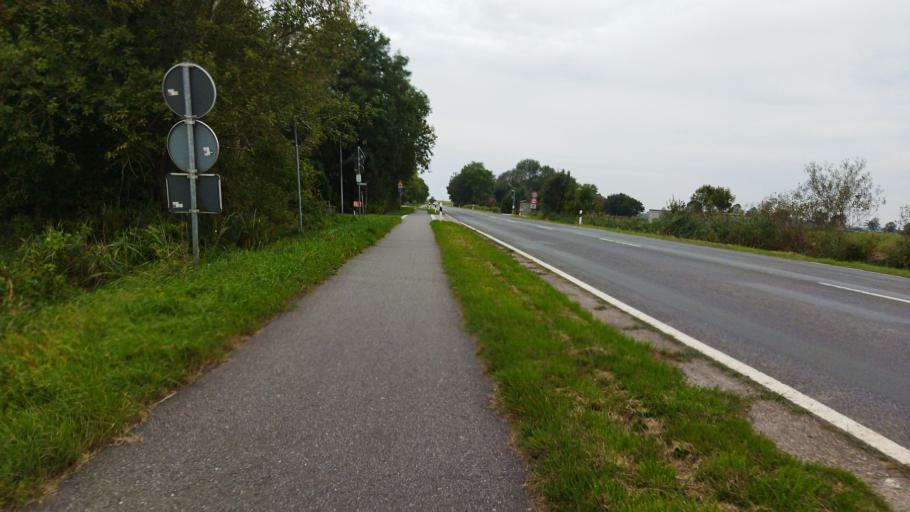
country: DE
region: Lower Saxony
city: Jemgum
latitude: 53.3250
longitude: 7.3125
